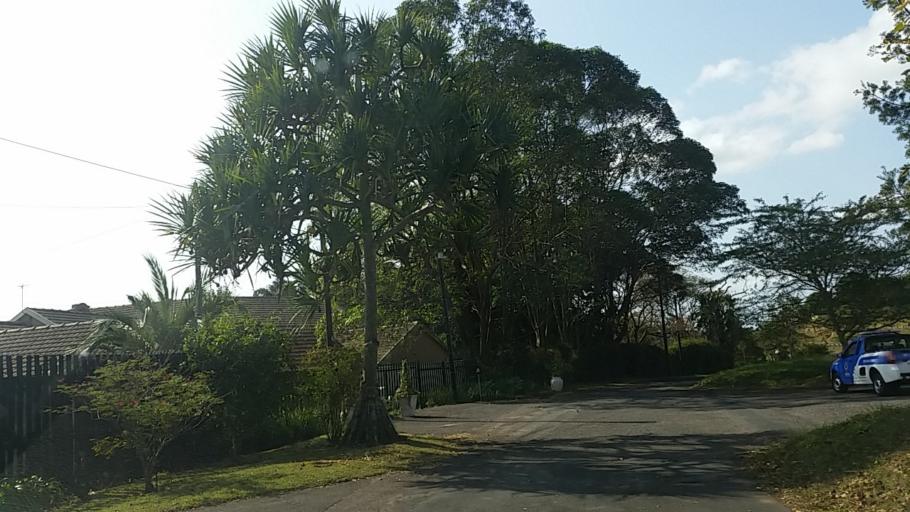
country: ZA
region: KwaZulu-Natal
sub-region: eThekwini Metropolitan Municipality
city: Berea
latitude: -29.8358
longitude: 30.9070
